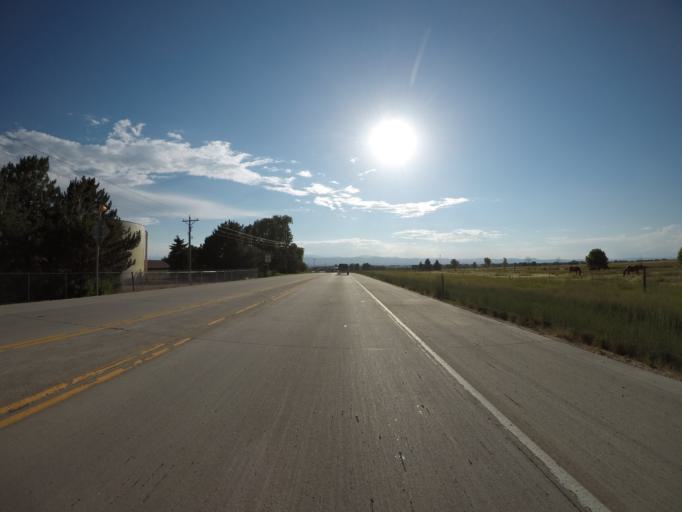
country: US
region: Colorado
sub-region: Weld County
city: Severance
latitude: 40.5816
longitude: -104.9107
